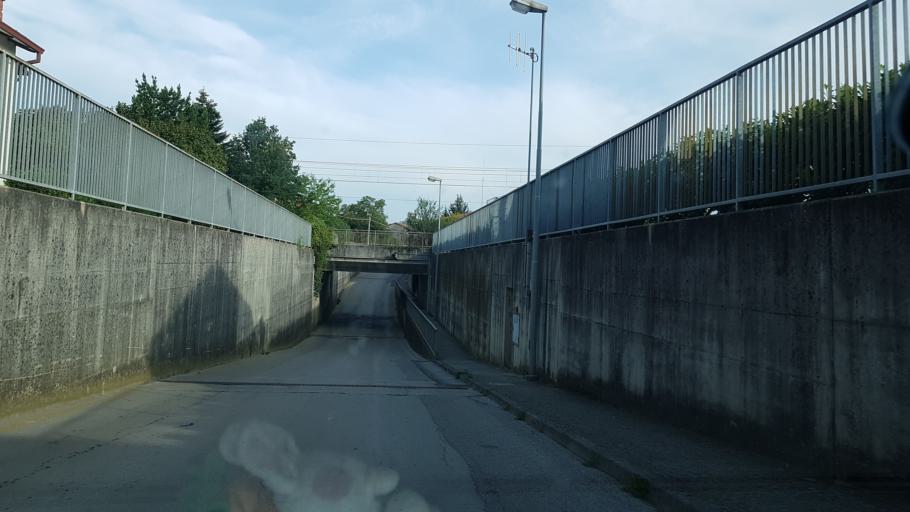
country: IT
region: Friuli Venezia Giulia
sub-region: Provincia di Gorizia
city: Mossa
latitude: 45.9385
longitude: 13.5749
